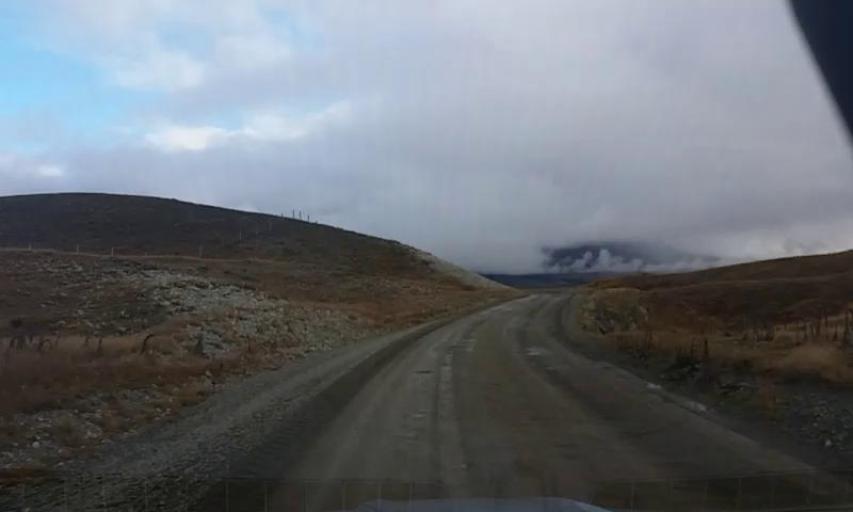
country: NZ
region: Canterbury
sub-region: Ashburton District
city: Methven
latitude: -43.6158
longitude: 171.1350
